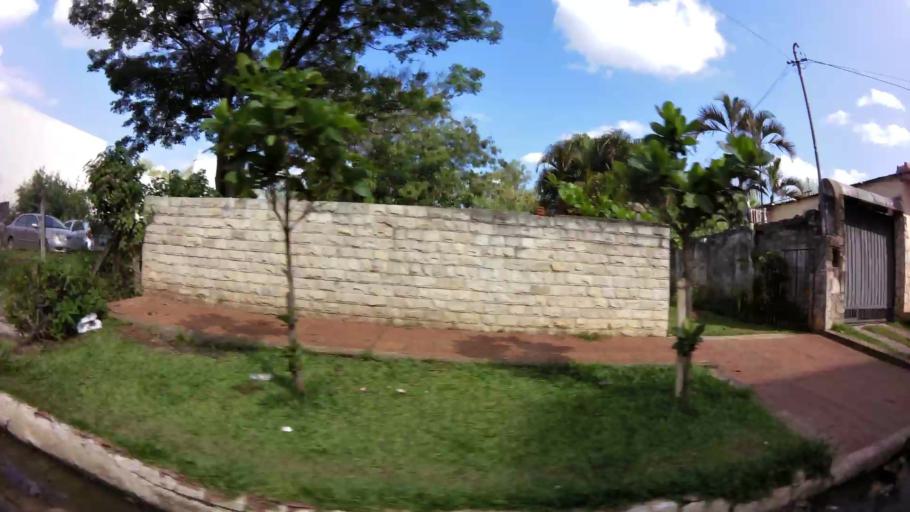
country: PY
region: Central
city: Fernando de la Mora
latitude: -25.3125
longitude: -57.5327
